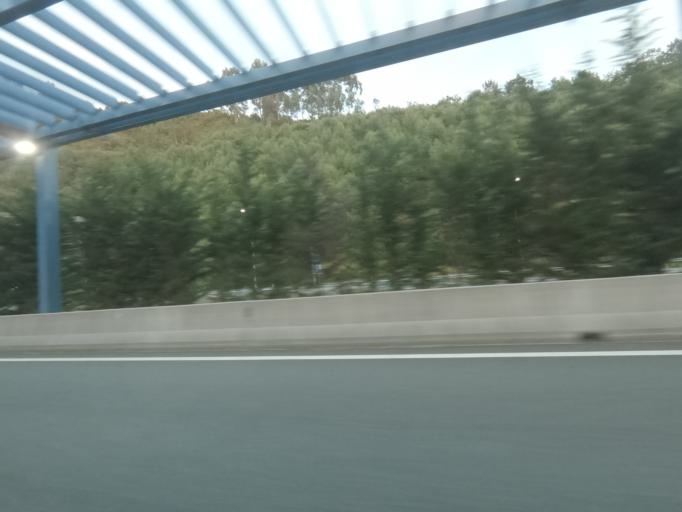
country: ES
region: Galicia
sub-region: Provincia de Pontevedra
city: Covelo
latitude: 42.1735
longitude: -8.3711
